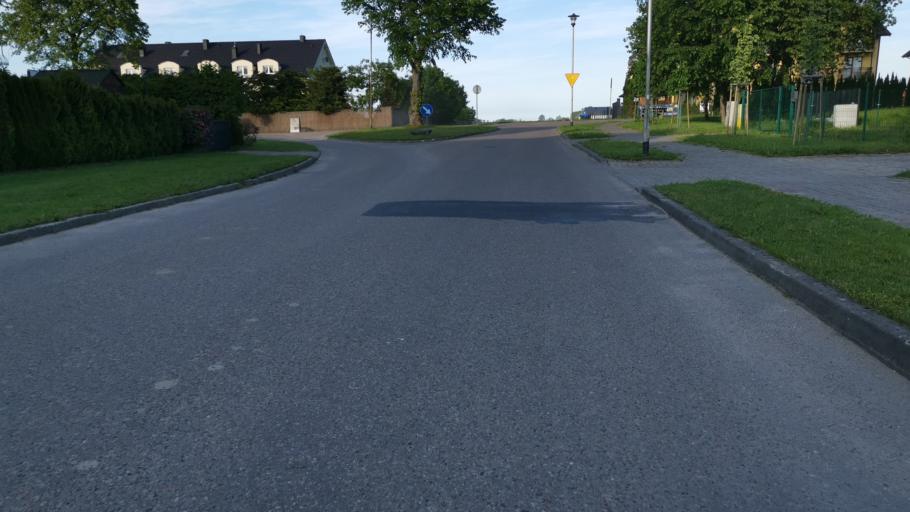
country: PL
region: West Pomeranian Voivodeship
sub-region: Powiat kolobrzeski
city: Ustronie Morskie
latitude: 54.2071
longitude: 15.7505
